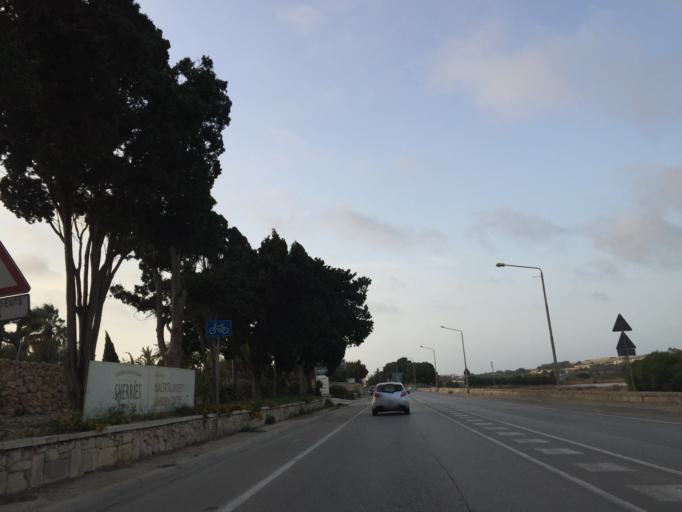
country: MT
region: Il-Mosta
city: Mosta
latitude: 35.9260
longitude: 14.4159
